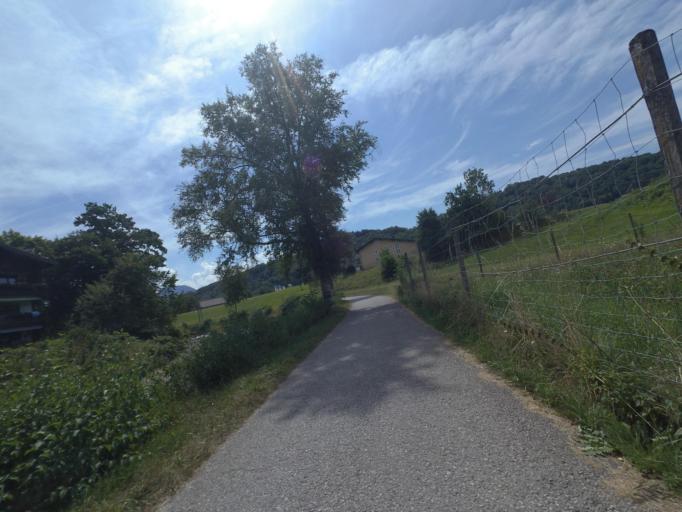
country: AT
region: Salzburg
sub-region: Politischer Bezirk Salzburg-Umgebung
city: Bergheim
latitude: 47.8447
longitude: 13.0409
